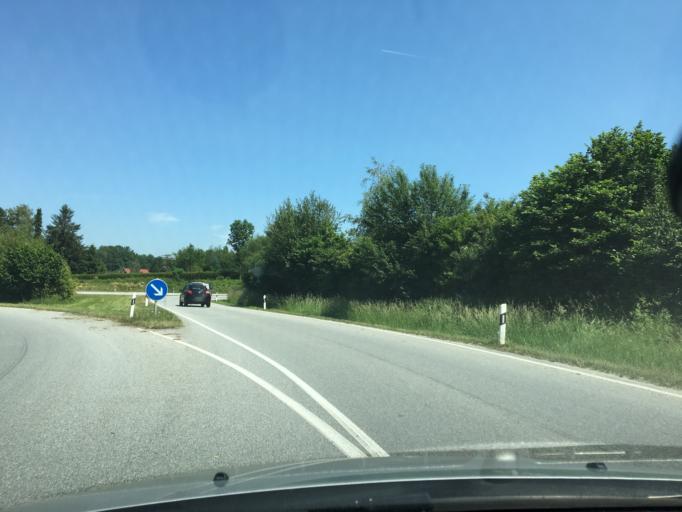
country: DE
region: Bavaria
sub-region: Lower Bavaria
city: Vilsbiburg
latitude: 48.4255
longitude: 12.3532
